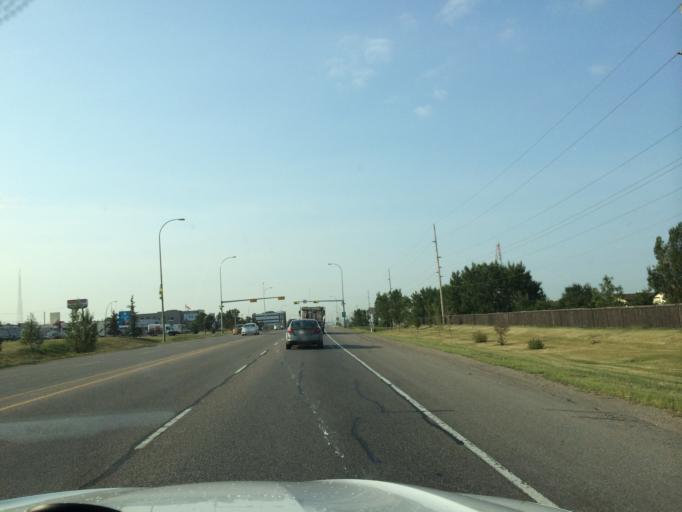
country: CA
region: Alberta
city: Calgary
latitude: 51.0568
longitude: -114.0020
